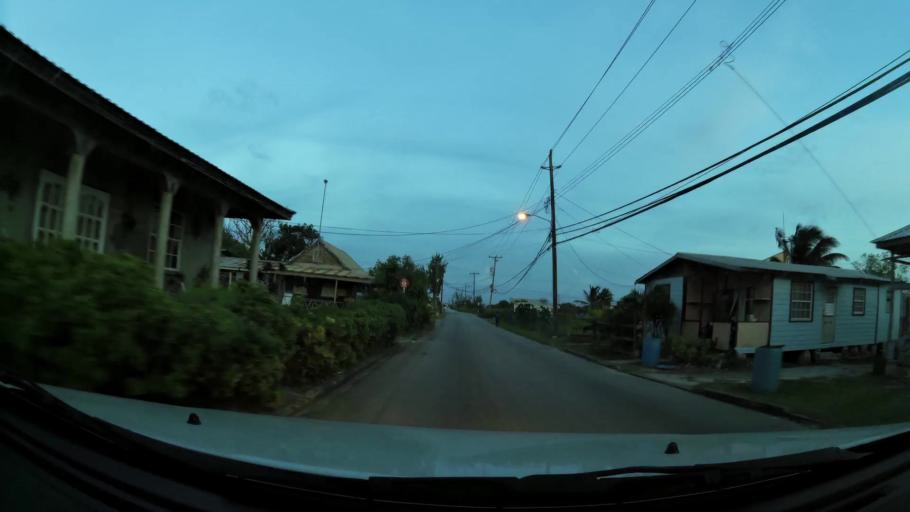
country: BB
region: Saint Philip
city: Crane
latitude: 13.1039
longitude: -59.4537
